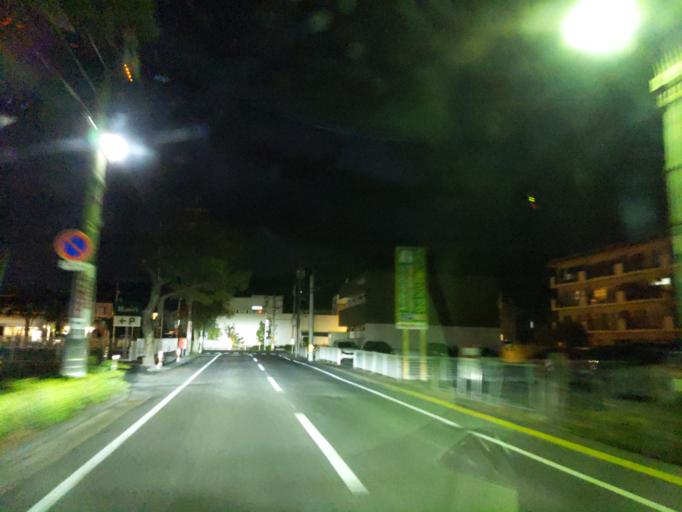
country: JP
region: Okayama
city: Okayama-shi
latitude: 34.6875
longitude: 133.9119
